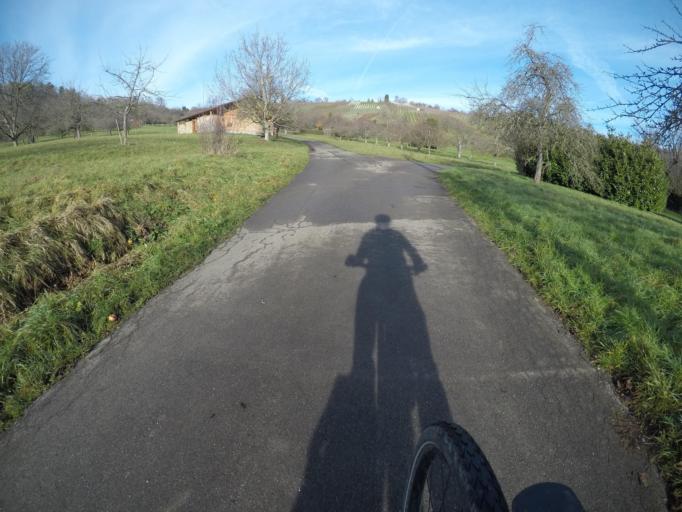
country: DE
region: Baden-Wuerttemberg
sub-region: Tuebingen Region
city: Metzingen
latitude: 48.5398
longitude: 9.3041
